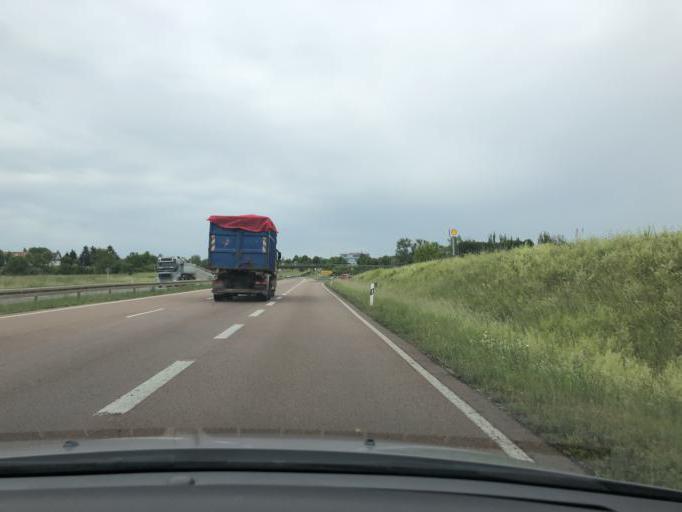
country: DE
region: Saxony-Anhalt
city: Burgwerben
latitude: 51.2023
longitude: 11.9969
